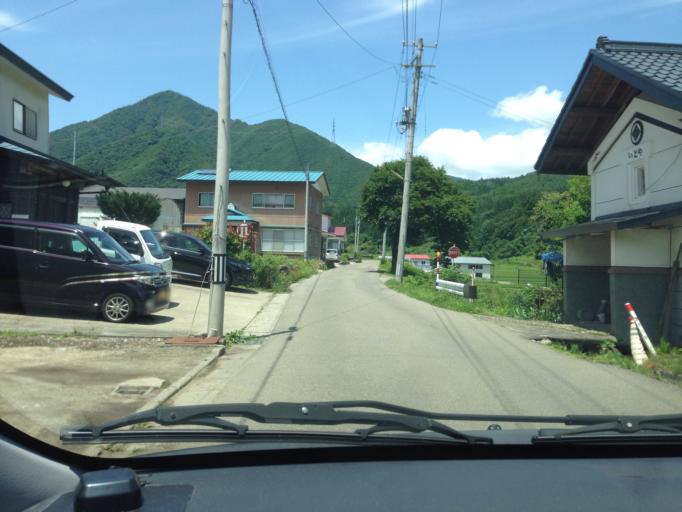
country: JP
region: Tochigi
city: Kuroiso
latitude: 37.2631
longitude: 139.8524
